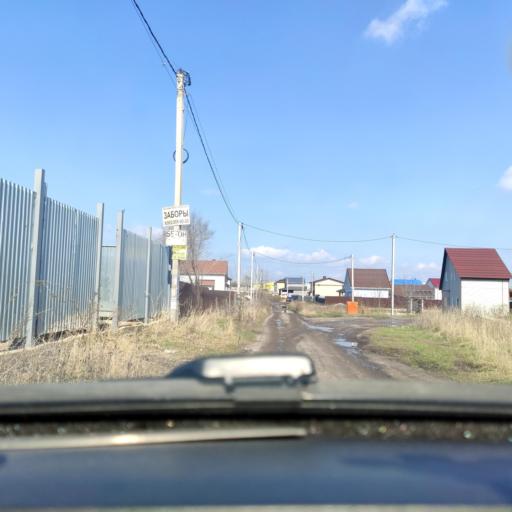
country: RU
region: Voronezj
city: Somovo
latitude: 51.6698
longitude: 39.3349
